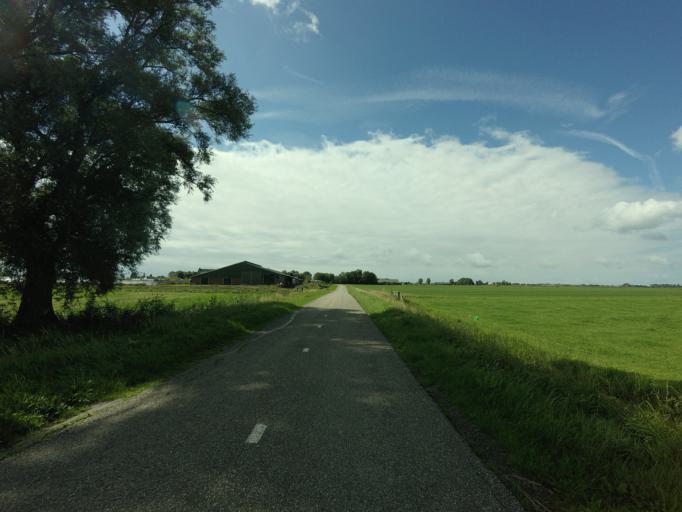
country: NL
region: Friesland
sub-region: Sudwest Fryslan
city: IJlst
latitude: 53.0275
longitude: 5.5792
